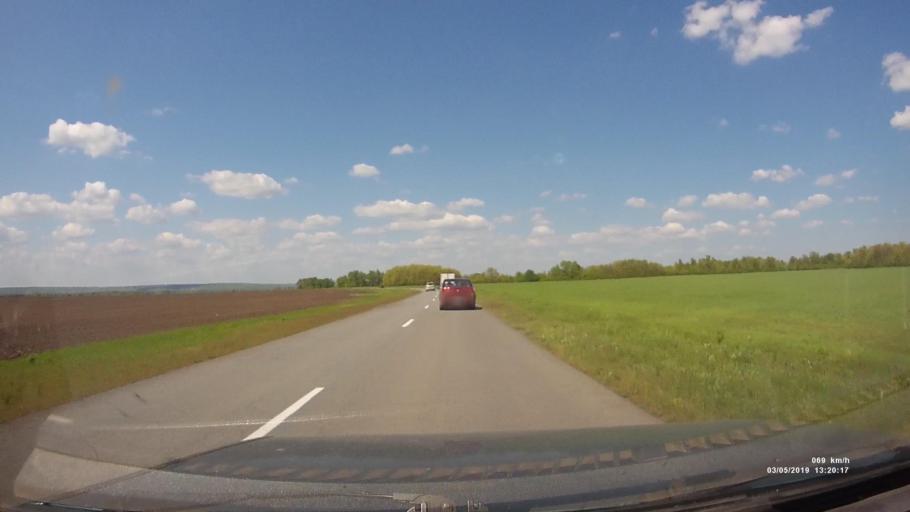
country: RU
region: Rostov
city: Semikarakorsk
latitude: 47.5447
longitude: 40.7541
